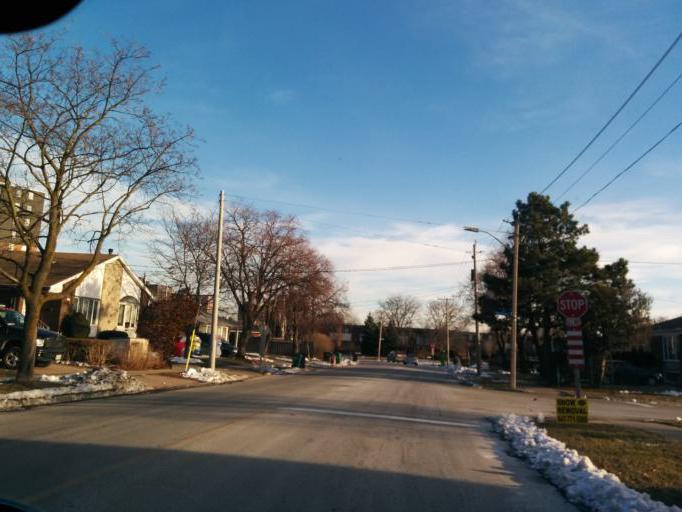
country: CA
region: Ontario
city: Etobicoke
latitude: 43.6099
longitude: -79.5932
